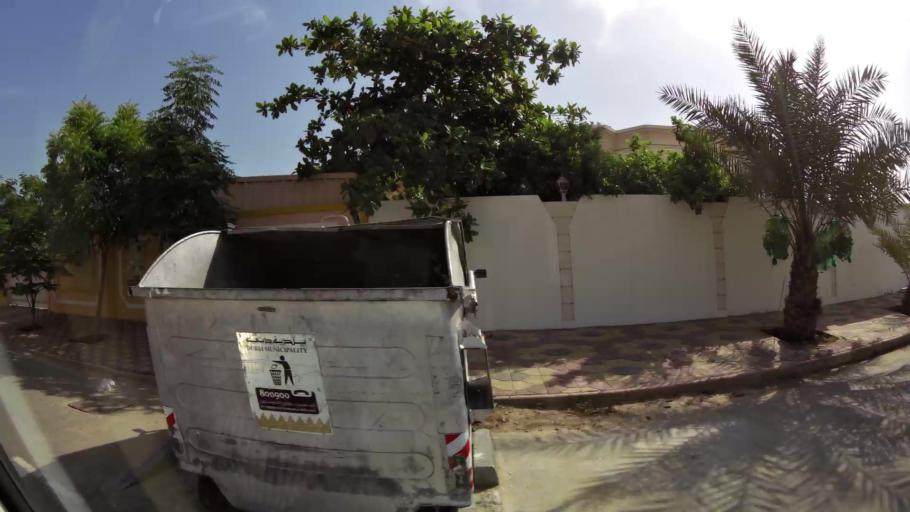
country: AE
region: Ash Shariqah
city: Sharjah
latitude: 25.2766
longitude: 55.3977
